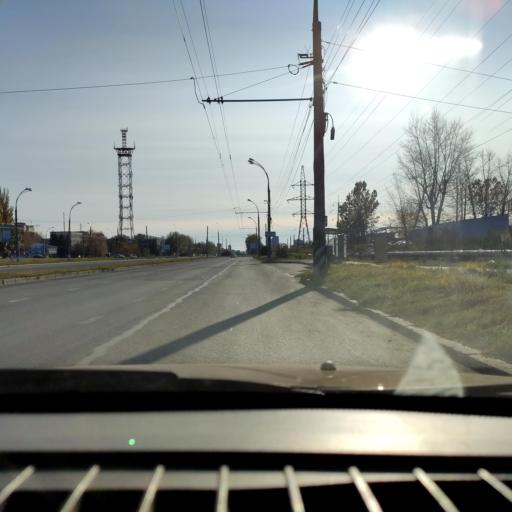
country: RU
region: Samara
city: Tol'yatti
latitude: 53.5329
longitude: 49.2618
